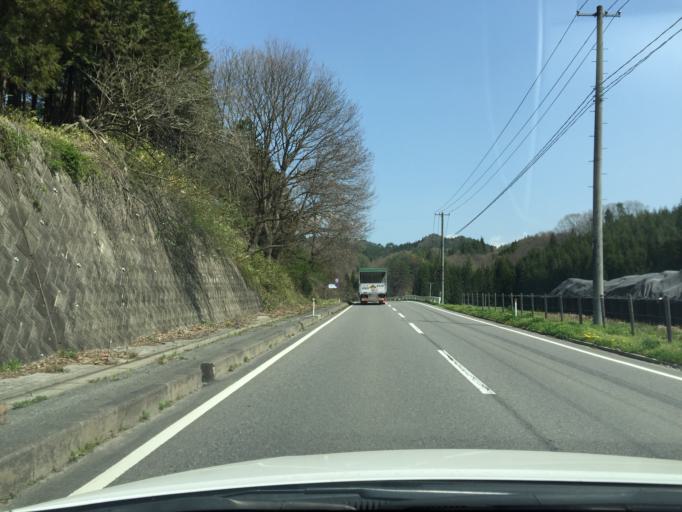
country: JP
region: Fukushima
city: Funehikimachi-funehiki
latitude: 37.4503
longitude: 140.6752
